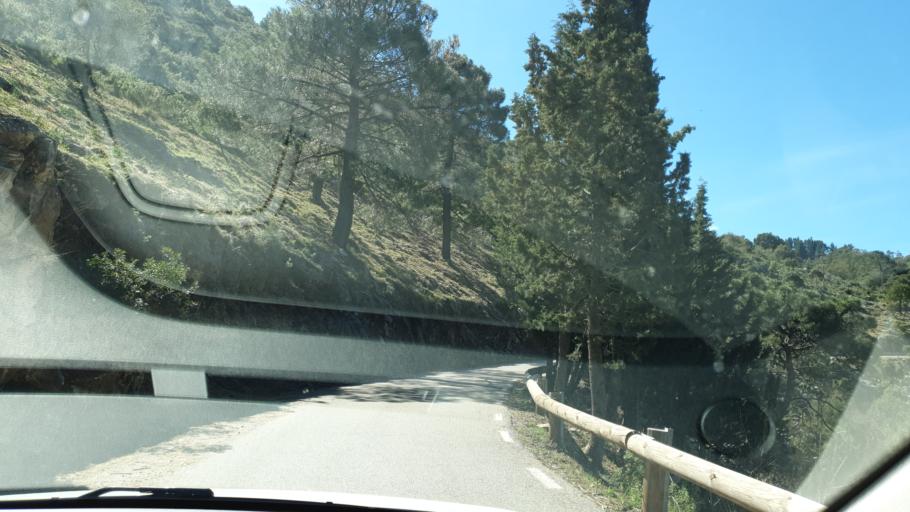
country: ES
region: Andalusia
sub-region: Provincia de Malaga
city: Ojen
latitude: 36.5841
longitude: -4.8825
